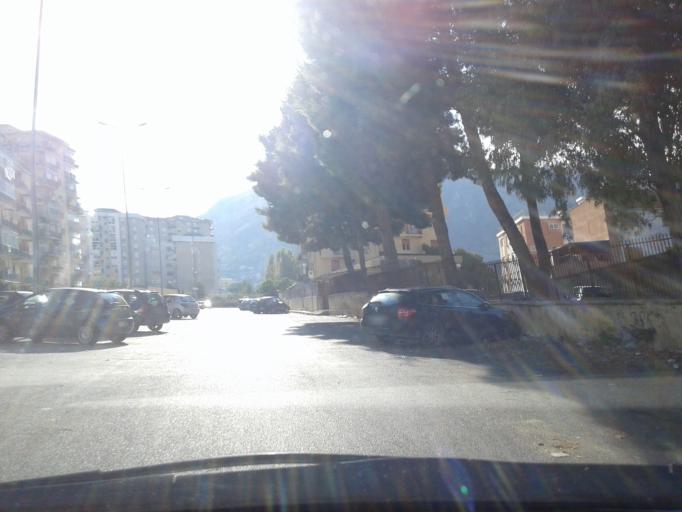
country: IT
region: Sicily
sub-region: Palermo
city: Monreale
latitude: 38.0995
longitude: 13.3194
